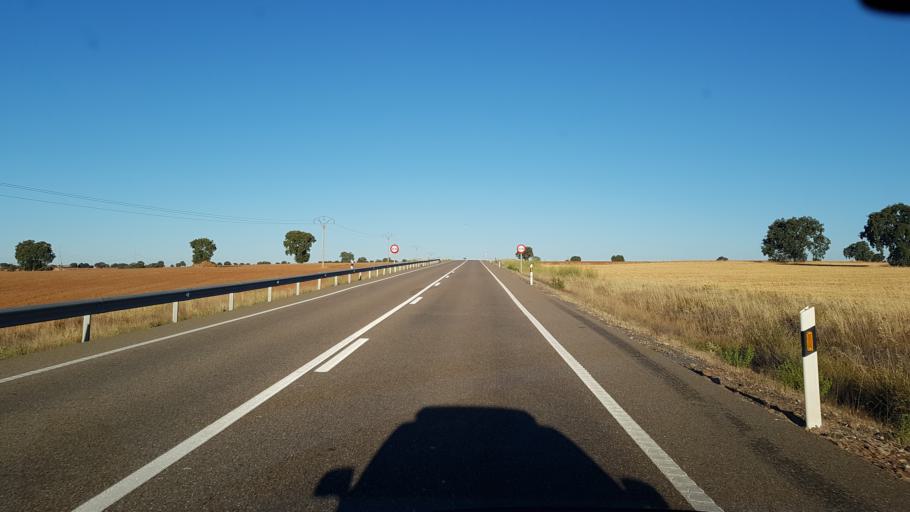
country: ES
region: Castille and Leon
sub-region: Provincia de Zamora
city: Palacios del Pan
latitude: 41.5463
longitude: -5.8907
